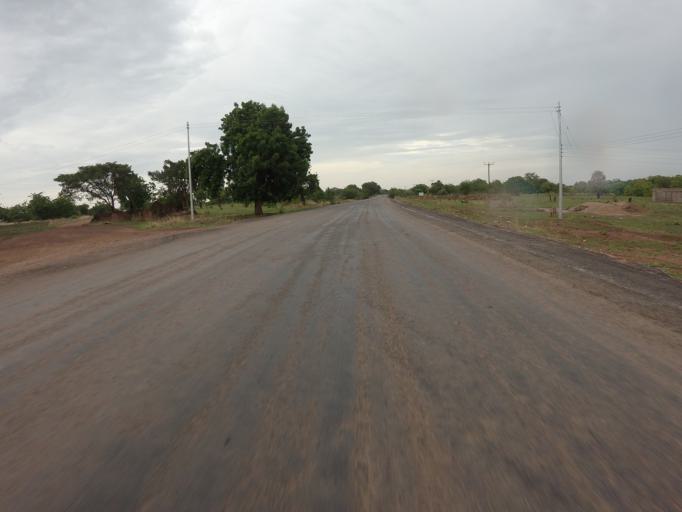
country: GH
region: Upper East
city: Bolgatanga
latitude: 10.8654
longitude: -0.6579
